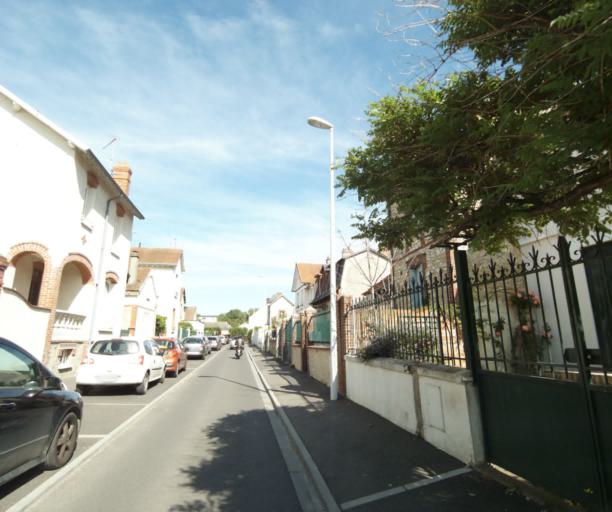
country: FR
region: Centre
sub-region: Departement d'Eure-et-Loir
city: Luisant
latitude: 48.4393
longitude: 1.4762
